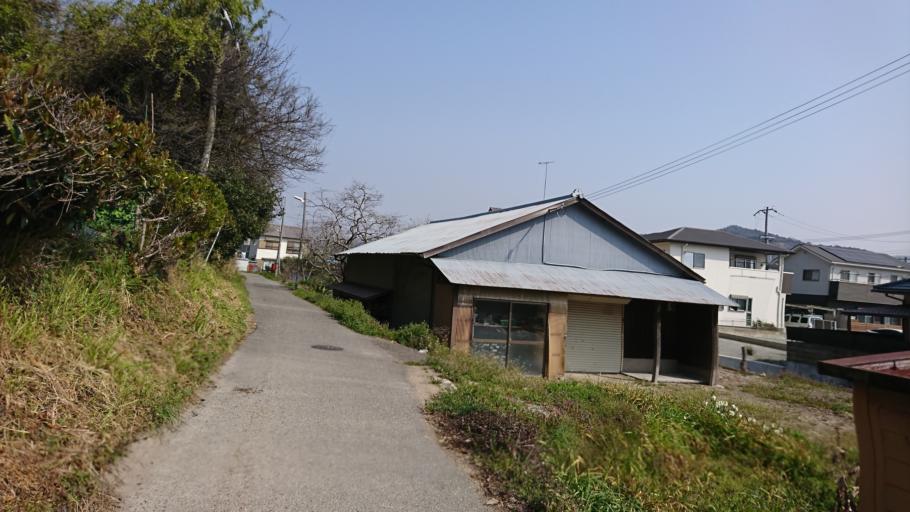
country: JP
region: Hyogo
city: Shirahamacho-usazakiminami
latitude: 34.7890
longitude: 134.7647
